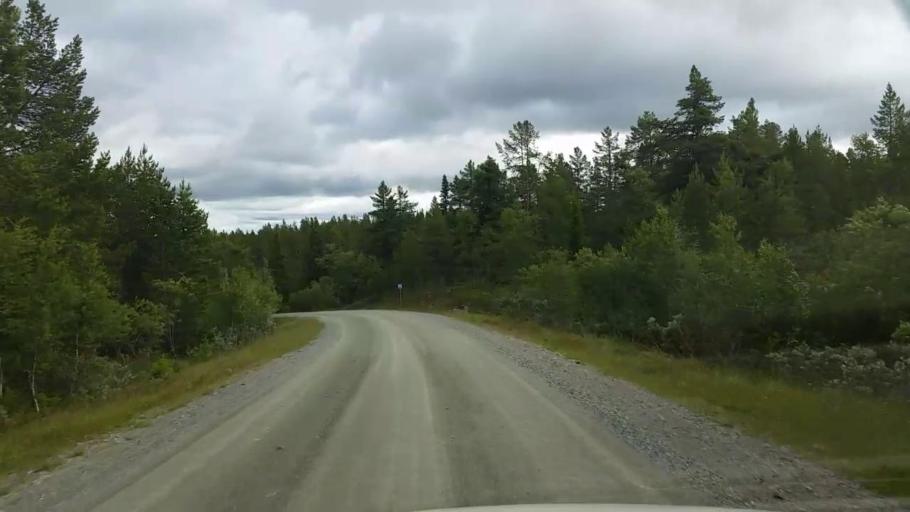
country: NO
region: Hedmark
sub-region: Engerdal
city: Engerdal
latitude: 62.3319
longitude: 12.6409
